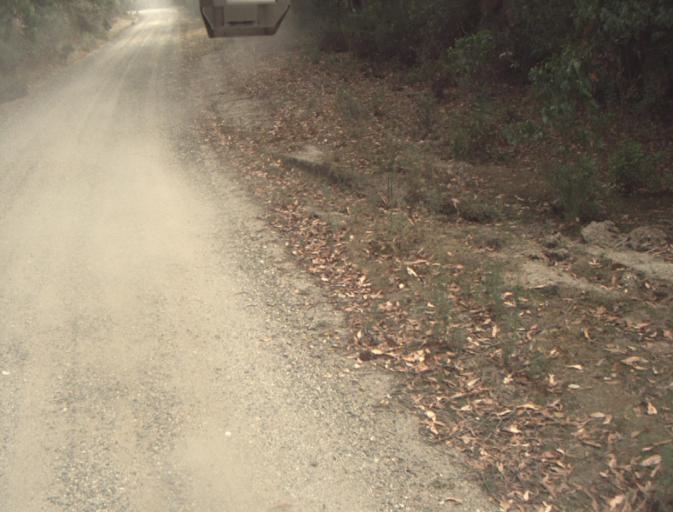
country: AU
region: Tasmania
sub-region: Launceston
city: Mayfield
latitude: -41.1577
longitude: 147.1730
